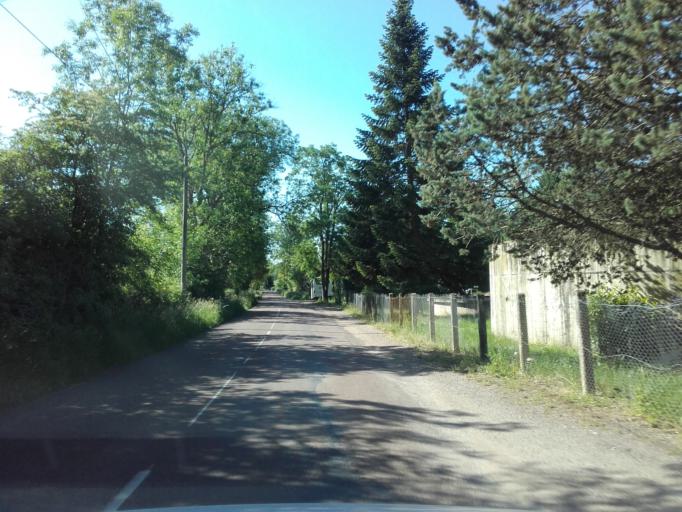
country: FR
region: Bourgogne
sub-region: Departement de la Cote-d'Or
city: Nolay
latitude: 46.9409
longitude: 4.6290
